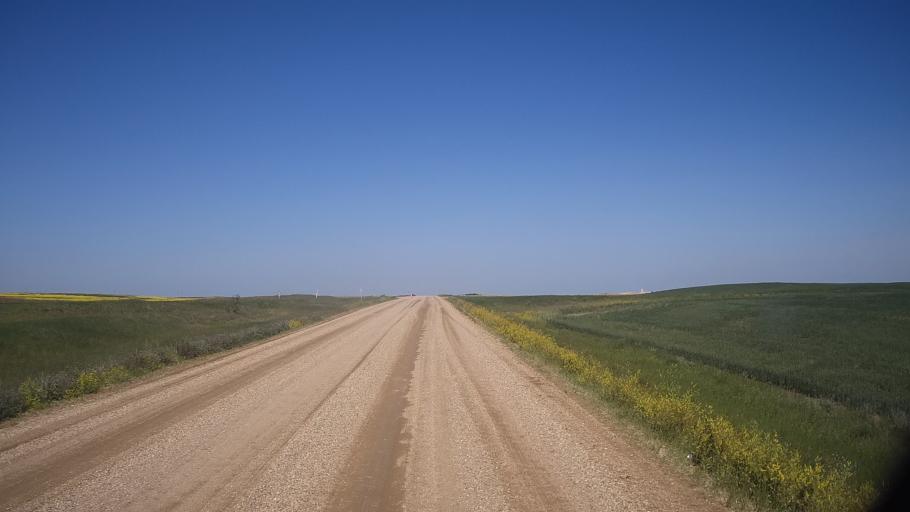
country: CA
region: Saskatchewan
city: Watrous
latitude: 51.8519
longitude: -105.9383
